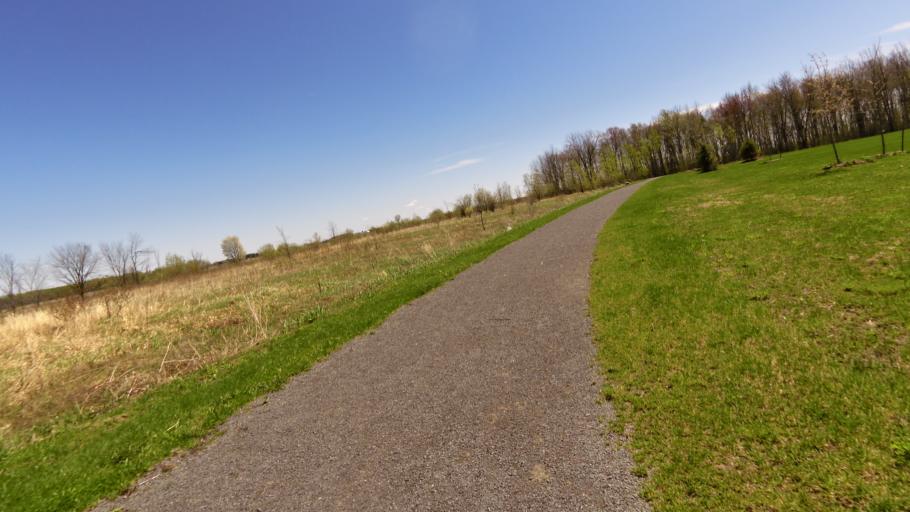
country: CA
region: Ontario
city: Clarence-Rockland
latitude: 45.4664
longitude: -75.4434
